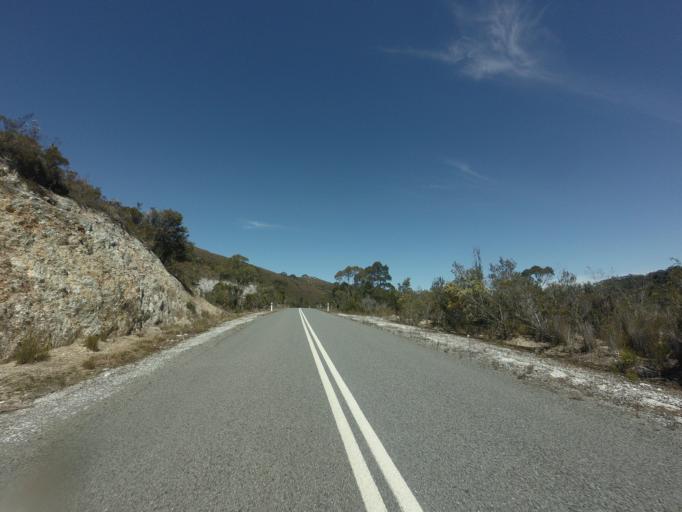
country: AU
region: Tasmania
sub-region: Huon Valley
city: Geeveston
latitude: -42.8212
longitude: 146.1238
